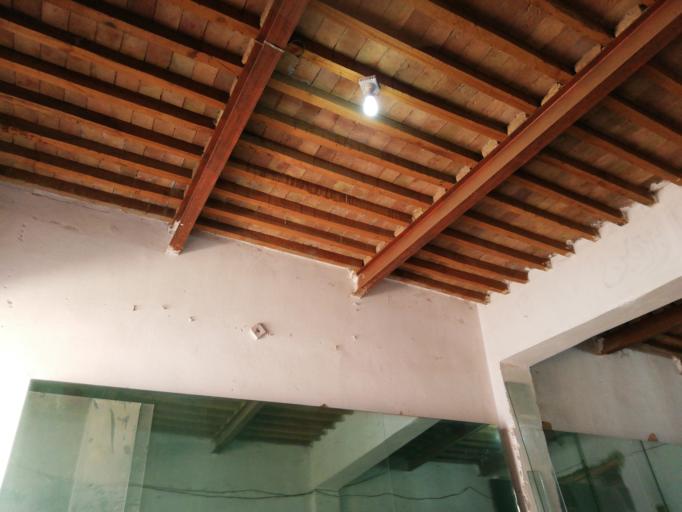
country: PK
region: Punjab
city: Mitha Tiwana
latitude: 32.3417
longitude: 71.8836
